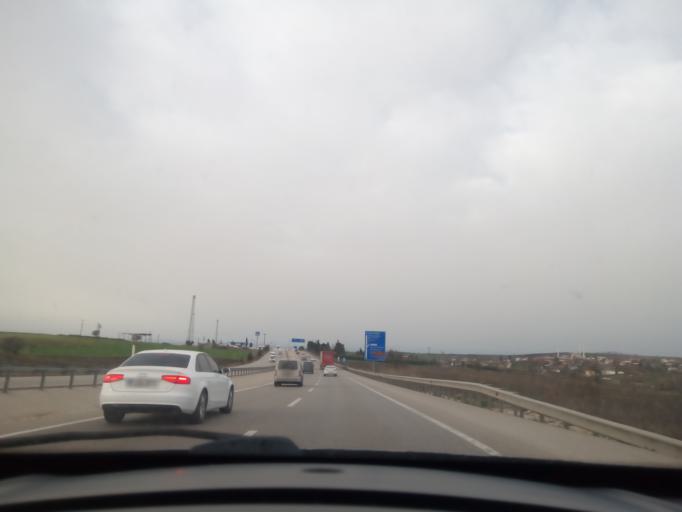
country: TR
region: Bursa
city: Mahmudiye
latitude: 40.2175
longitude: 28.6328
